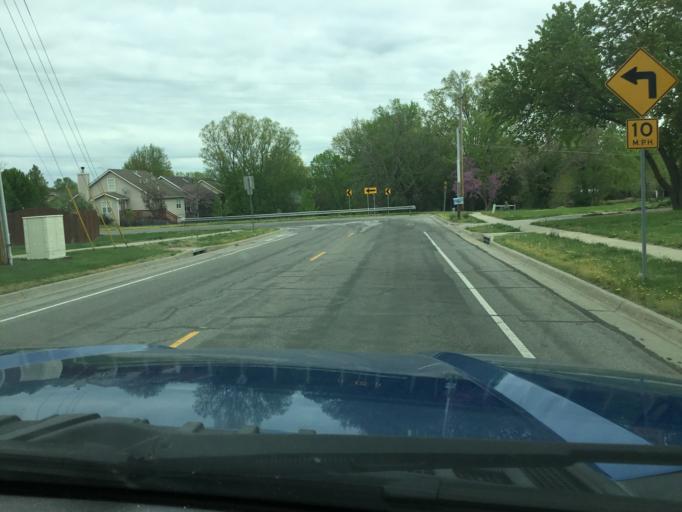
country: US
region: Kansas
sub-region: Douglas County
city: Lawrence
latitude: 38.9929
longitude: -95.2512
